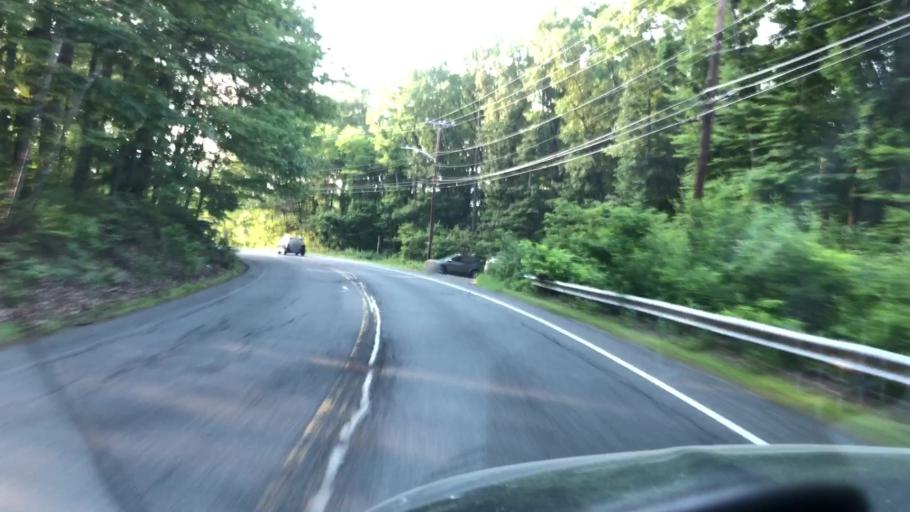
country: US
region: Massachusetts
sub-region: Hampden County
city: Holyoke
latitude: 42.2298
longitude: -72.6471
